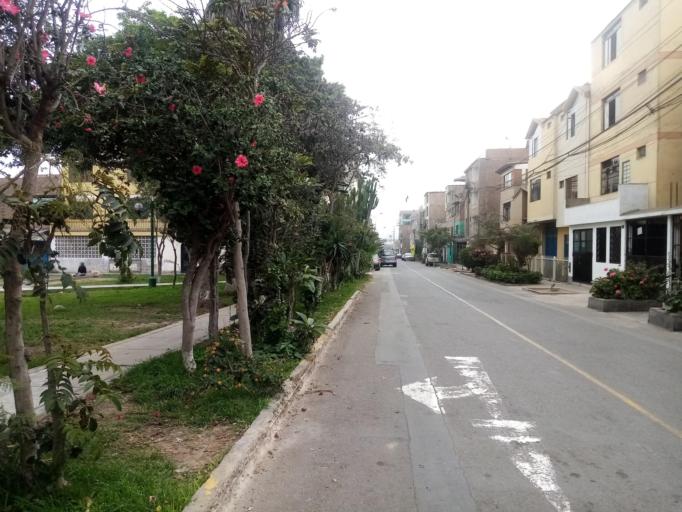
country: PE
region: Lima
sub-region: Lima
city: Vitarte
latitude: -12.0441
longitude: -76.9546
